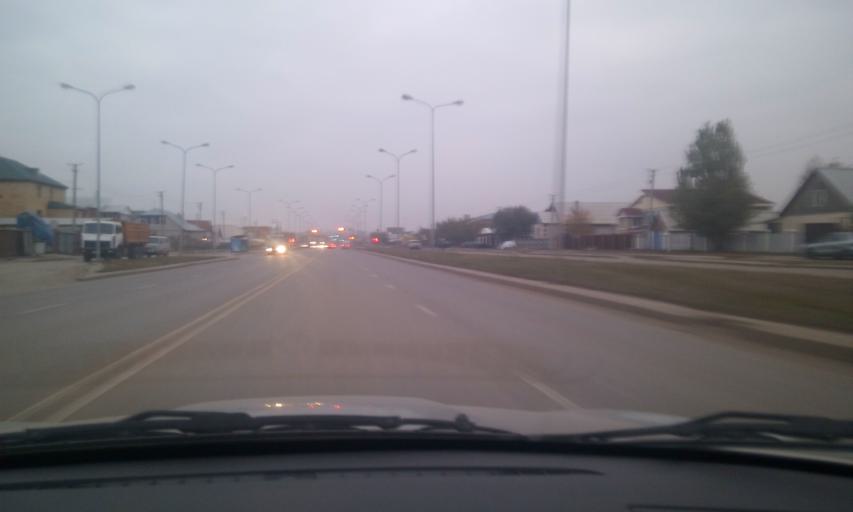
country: KZ
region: Astana Qalasy
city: Astana
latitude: 51.1352
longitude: 71.5092
